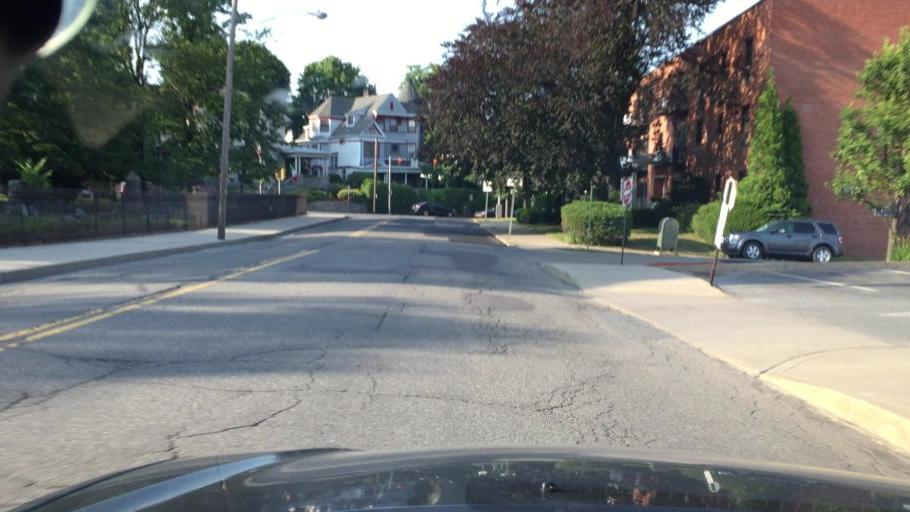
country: US
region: Pennsylvania
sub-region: Luzerne County
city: Hazleton
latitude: 40.9589
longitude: -75.9767
